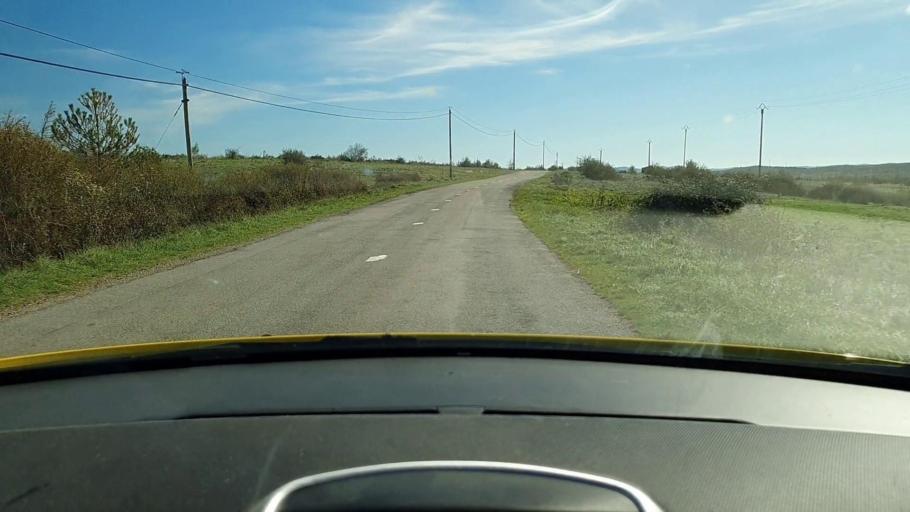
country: FR
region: Languedoc-Roussillon
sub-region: Departement du Gard
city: Aveze
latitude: 43.9569
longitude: 3.4128
